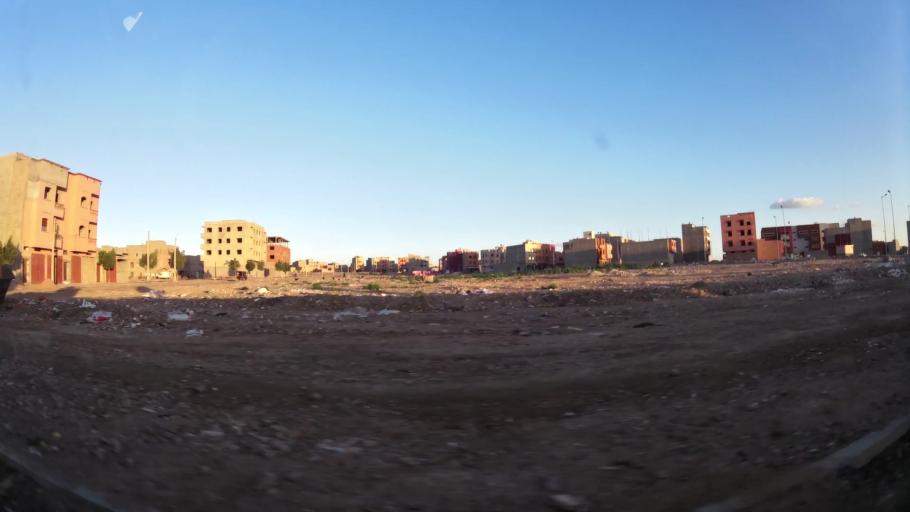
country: MA
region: Marrakech-Tensift-Al Haouz
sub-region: Kelaa-Des-Sraghna
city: Sidi Abdallah
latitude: 32.2422
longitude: -7.9428
